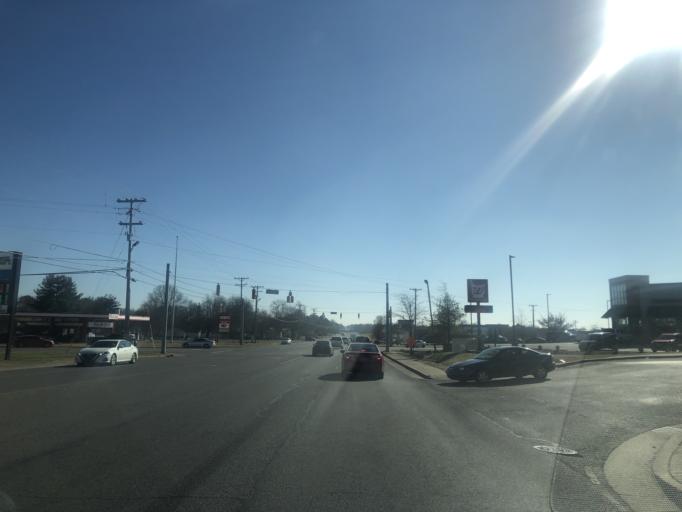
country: US
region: Tennessee
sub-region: Rutherford County
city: Smyrna
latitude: 35.9601
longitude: -86.5212
